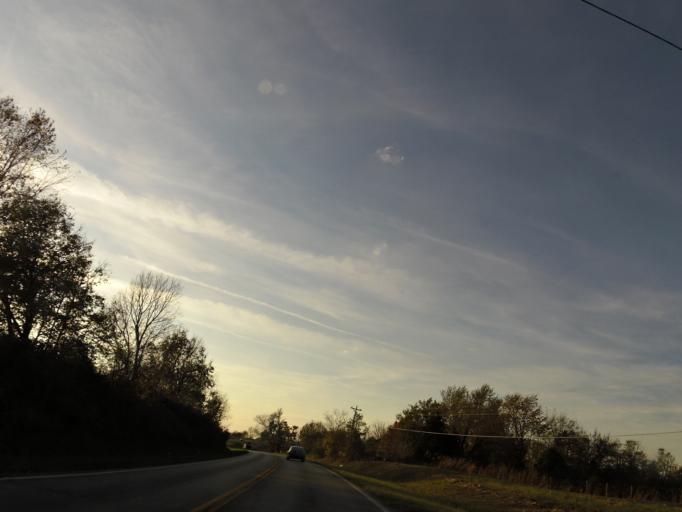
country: US
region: Kentucky
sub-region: Garrard County
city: Lancaster
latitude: 37.6737
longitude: -84.6393
